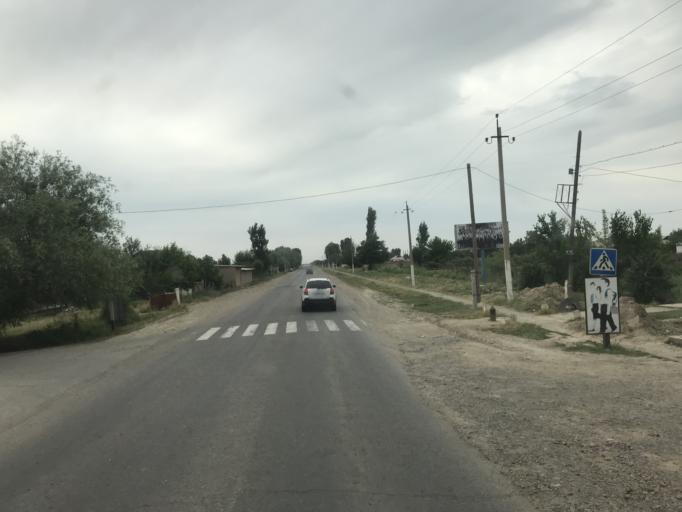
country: KZ
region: Ongtustik Qazaqstan
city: Asykata
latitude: 40.9039
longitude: 68.3559
